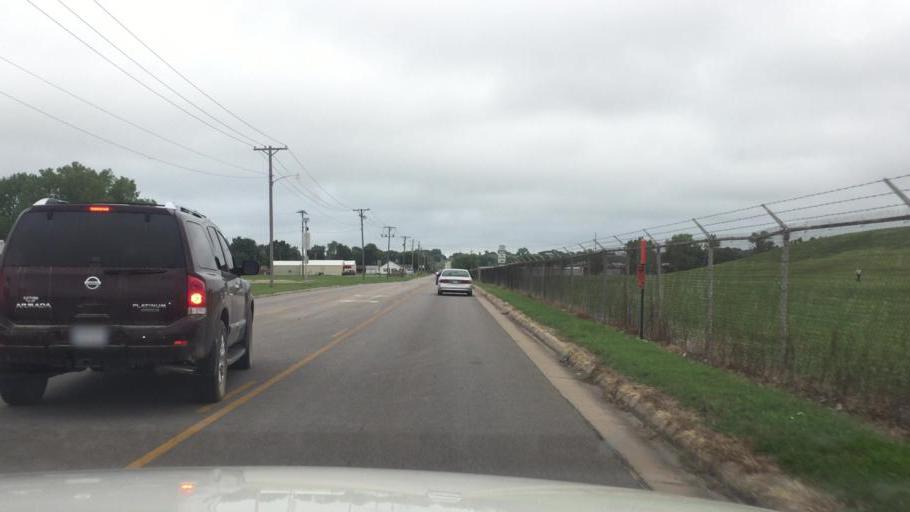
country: US
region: Kansas
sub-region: Montgomery County
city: Coffeyville
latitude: 37.0440
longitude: -95.6473
